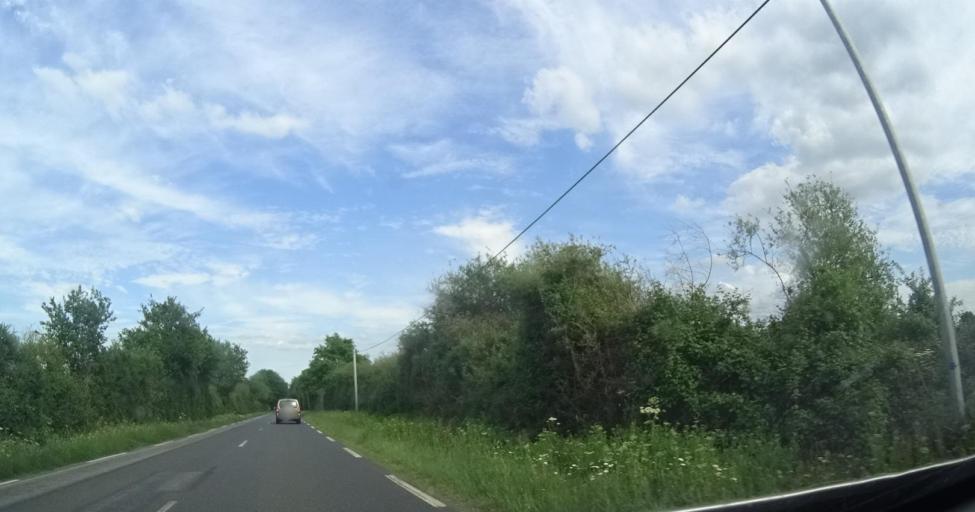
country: FR
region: Pays de la Loire
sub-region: Departement de la Loire-Atlantique
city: Fay-de-Bretagne
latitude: 47.4133
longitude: -1.7757
